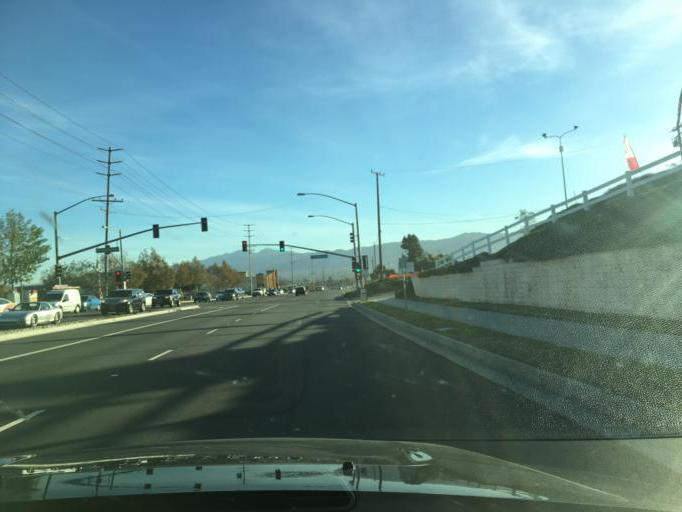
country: US
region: California
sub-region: Riverside County
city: Norco
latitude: 33.9352
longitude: -117.5574
